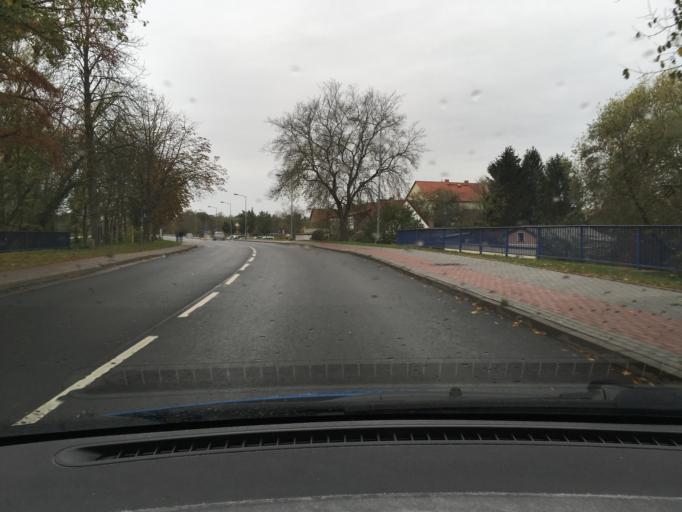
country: DE
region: Saxony-Anhalt
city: Rosslau
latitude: 51.8866
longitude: 12.2543
